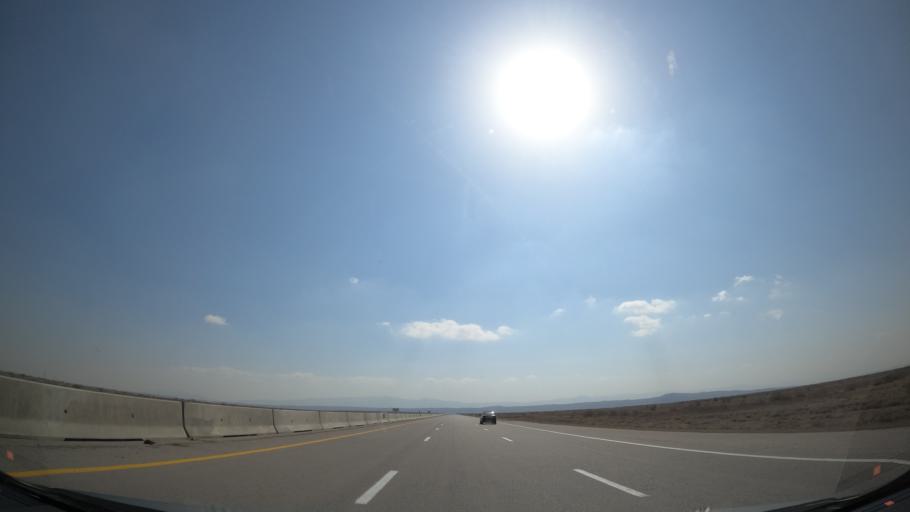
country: IR
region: Alborz
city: Nazarabad
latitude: 35.8597
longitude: 50.4798
